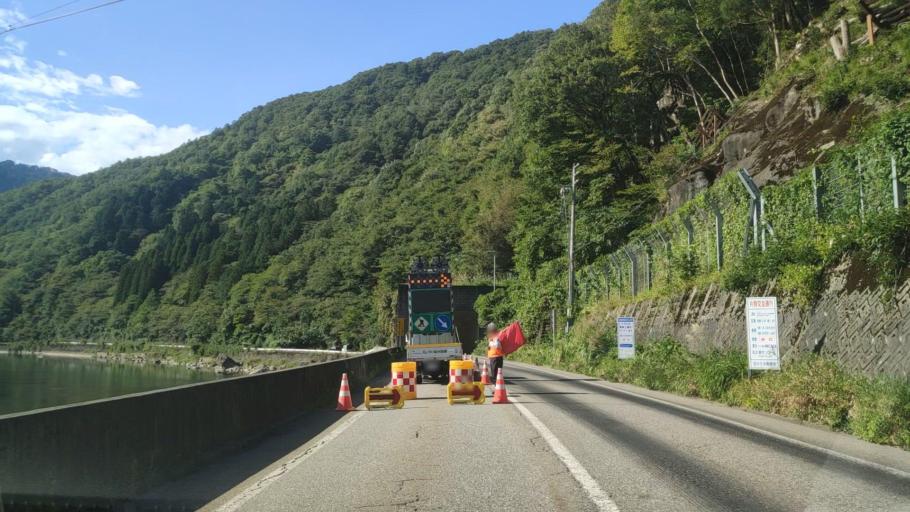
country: JP
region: Gifu
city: Takayama
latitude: 36.2772
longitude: 137.1363
